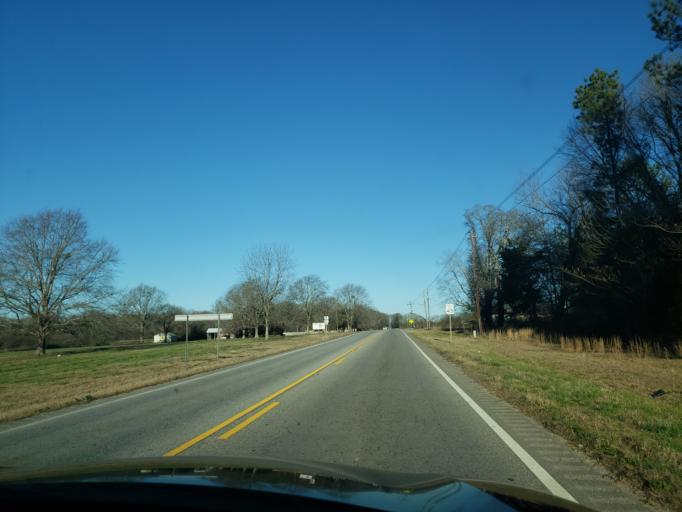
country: US
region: Alabama
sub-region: Lee County
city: Auburn
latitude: 32.6001
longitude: -85.5803
